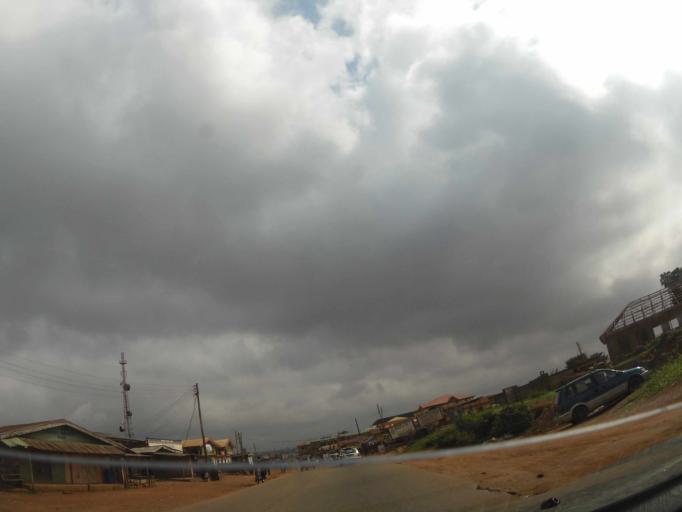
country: NG
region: Oyo
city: Ibadan
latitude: 7.4409
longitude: 3.9511
